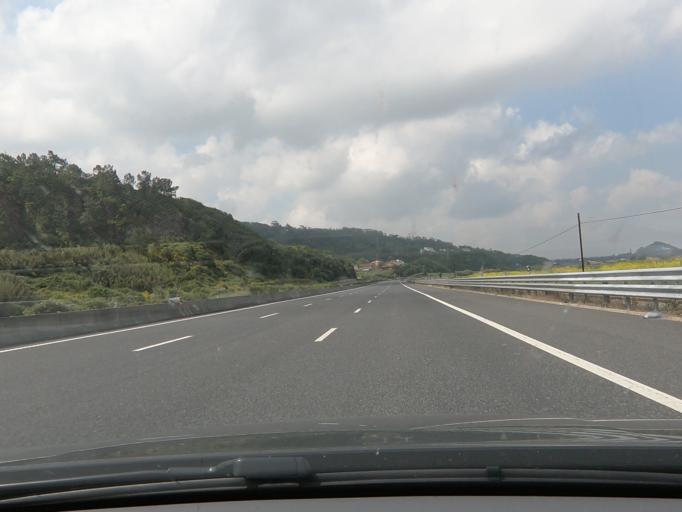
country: PT
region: Leiria
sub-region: Nazare
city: Nazare
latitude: 39.5613
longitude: -9.0434
